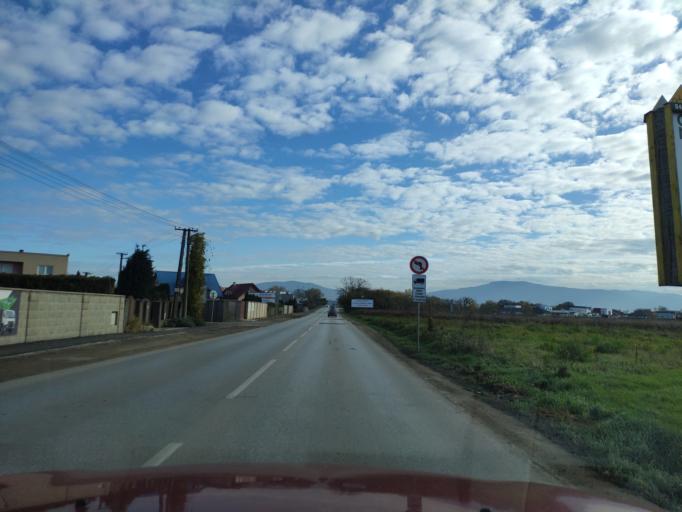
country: SK
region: Kosicky
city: Kosice
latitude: 48.6711
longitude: 21.3065
